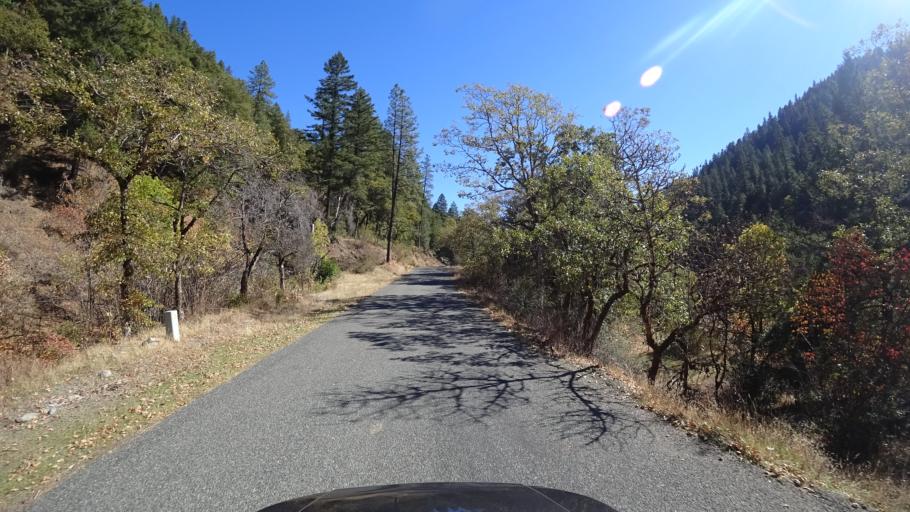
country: US
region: California
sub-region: Humboldt County
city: Willow Creek
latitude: 41.2857
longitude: -123.3622
